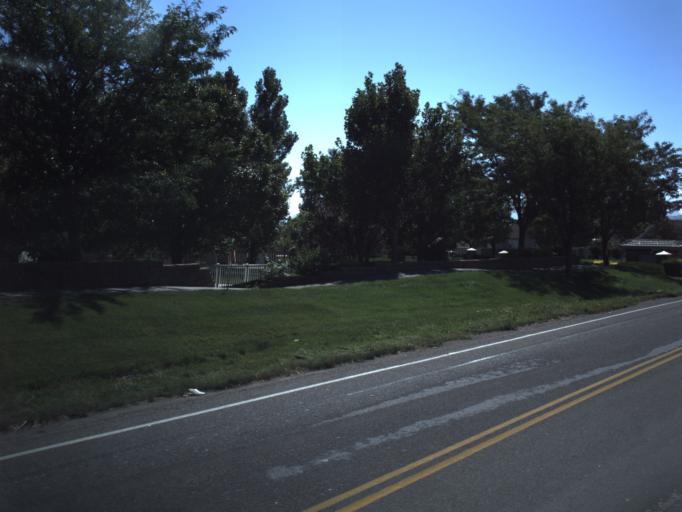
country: US
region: Utah
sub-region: Utah County
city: Saratoga Springs
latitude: 40.3452
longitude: -111.9163
